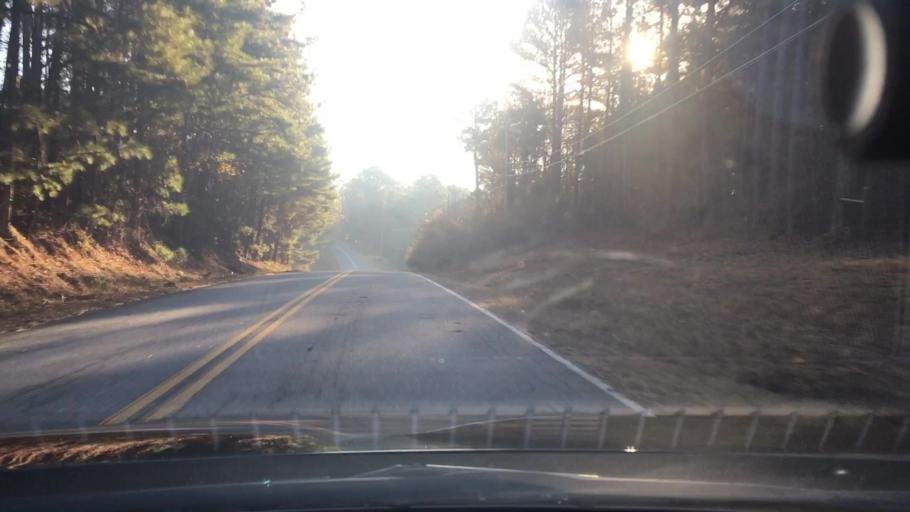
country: US
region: Georgia
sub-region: Spalding County
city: Experiment
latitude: 33.2621
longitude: -84.3013
